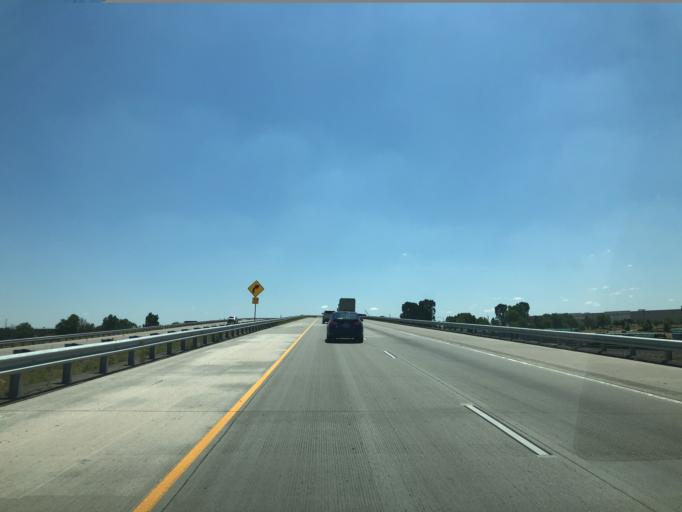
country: US
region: Colorado
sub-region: Adams County
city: Aurora
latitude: 39.7539
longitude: -104.7570
